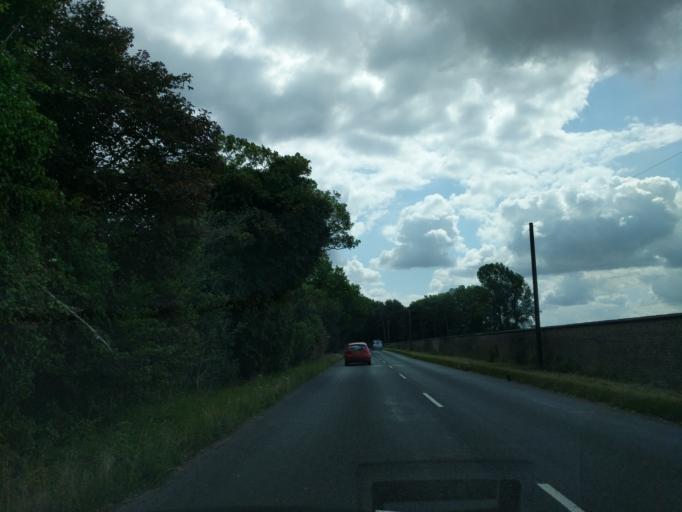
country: GB
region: England
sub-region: Cambridgeshire
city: Isleham
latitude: 52.2971
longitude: 0.4454
